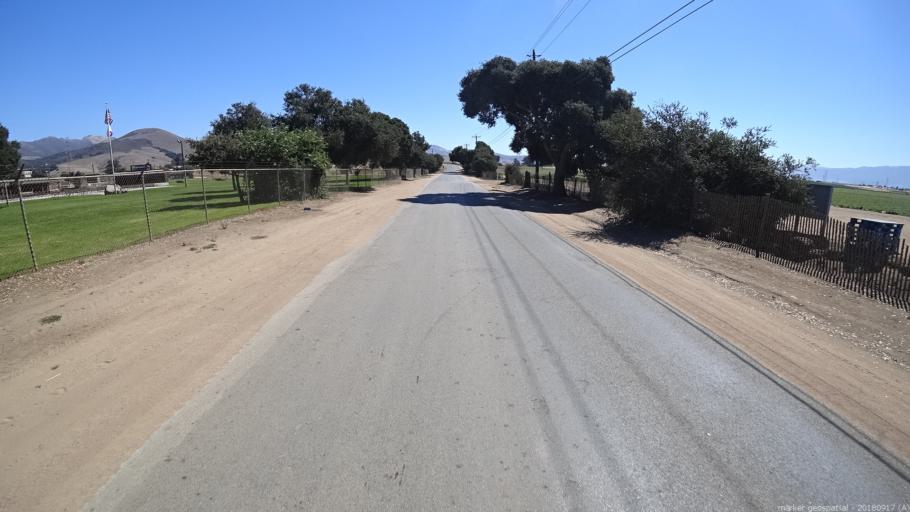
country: US
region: California
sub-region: Monterey County
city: Salinas
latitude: 36.7321
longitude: -121.6060
